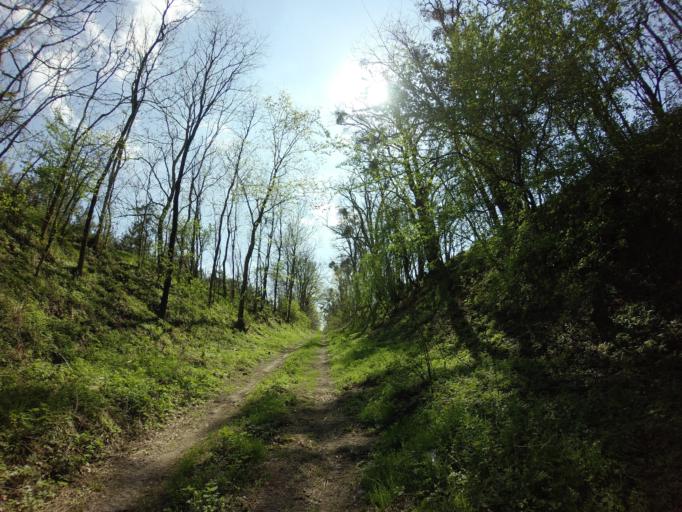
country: PL
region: West Pomeranian Voivodeship
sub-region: Powiat stargardzki
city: Suchan
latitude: 53.2131
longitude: 15.3029
